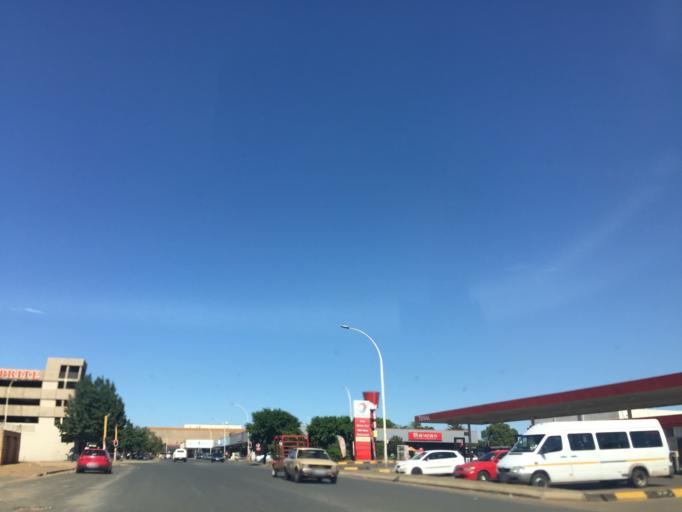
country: ZA
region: Gauteng
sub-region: Sedibeng District Municipality
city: Vanderbijlpark
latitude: -26.6977
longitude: 27.8397
